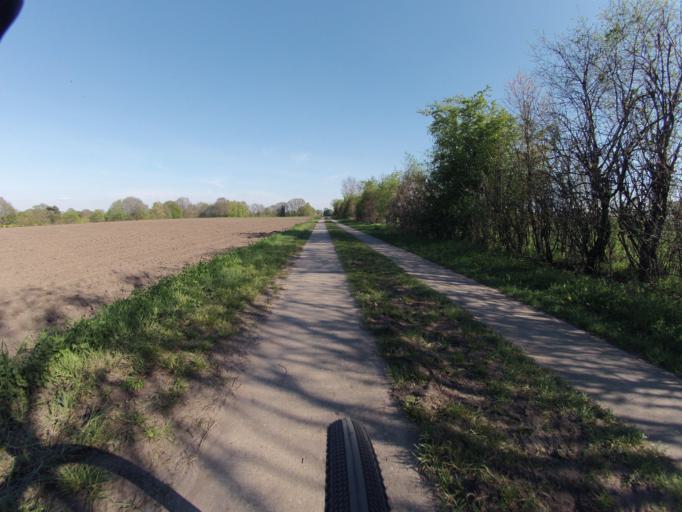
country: DE
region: Lower Saxony
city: Quendorf
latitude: 52.3374
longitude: 7.1906
